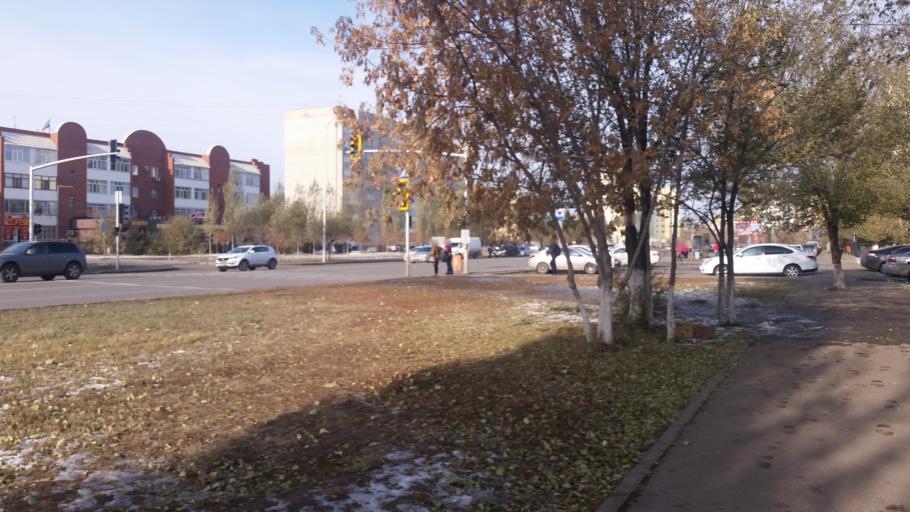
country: KZ
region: Astana Qalasy
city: Astana
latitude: 51.1547
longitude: 71.4793
